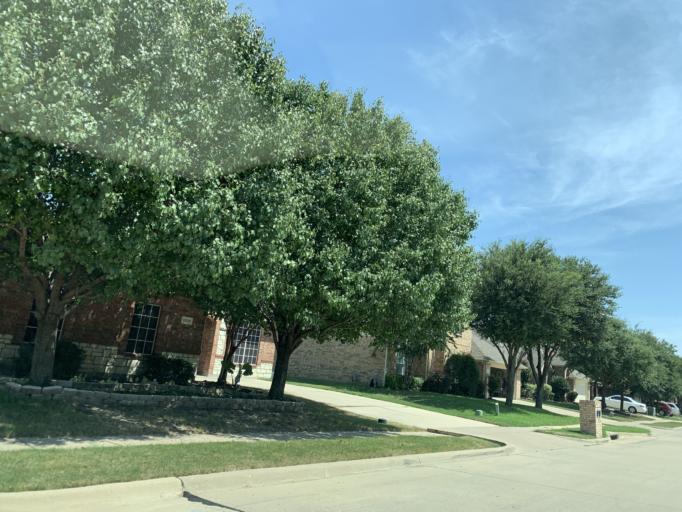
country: US
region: Texas
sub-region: Dallas County
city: Cedar Hill
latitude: 32.6455
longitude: -97.0149
